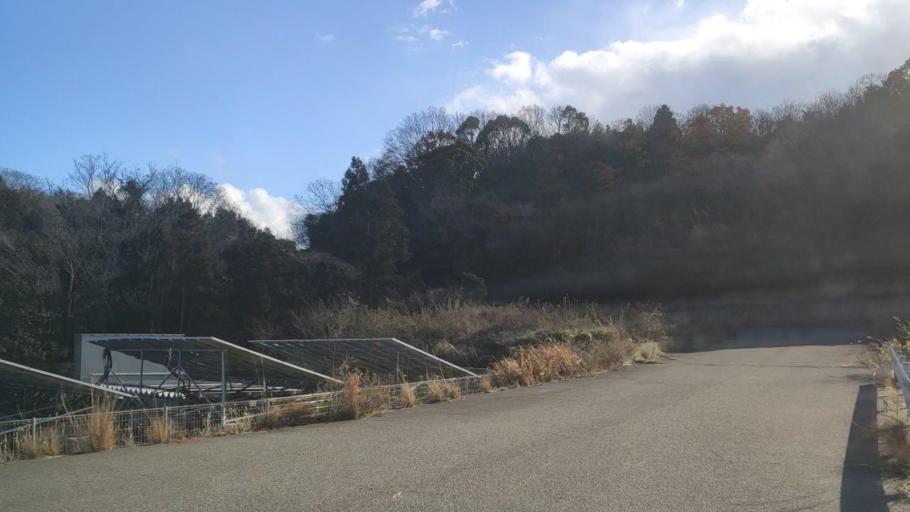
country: JP
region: Hiroshima
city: Innoshima
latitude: 34.2161
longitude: 133.1252
